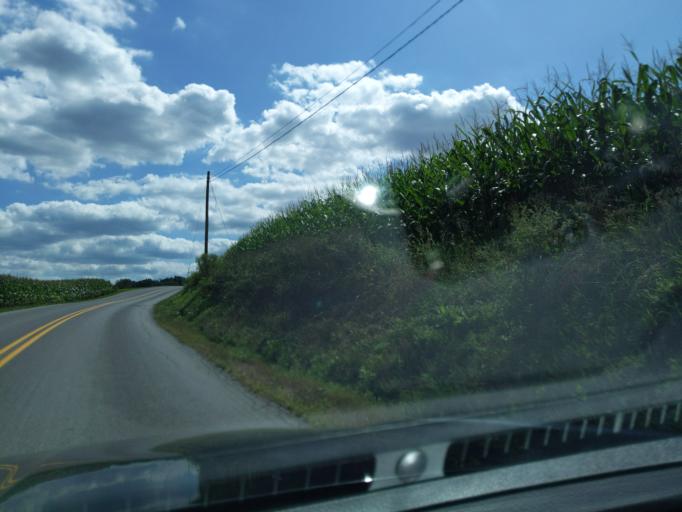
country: US
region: Pennsylvania
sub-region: Blair County
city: Tyrone
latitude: 40.6274
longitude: -78.2280
